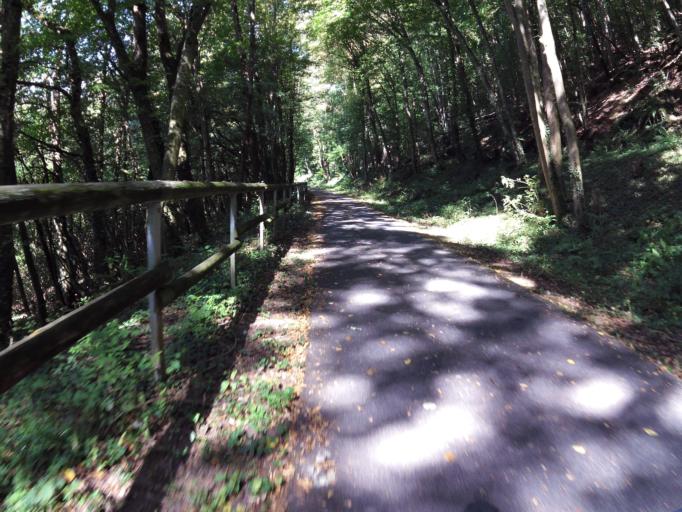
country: LU
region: Grevenmacher
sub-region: Canton d'Echternach
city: Rosport
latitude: 49.7674
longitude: 6.5198
